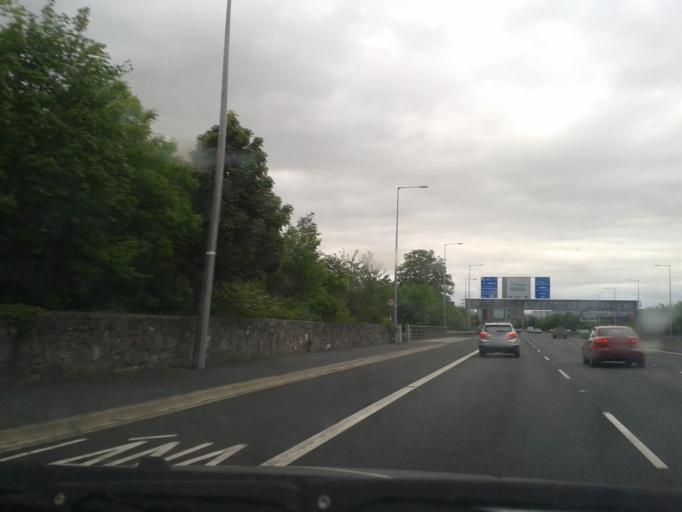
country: IE
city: Palmerstown
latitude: 53.3571
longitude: -6.4031
